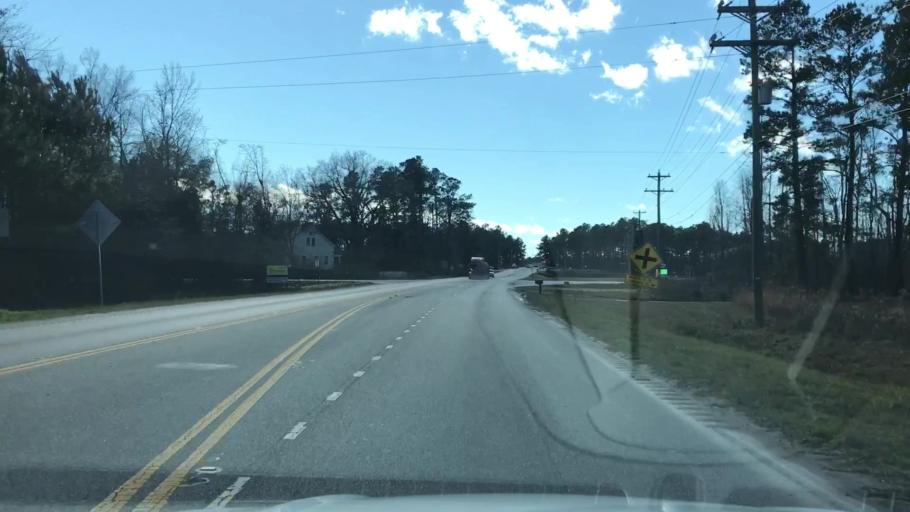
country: US
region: South Carolina
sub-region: Dorchester County
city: Summerville
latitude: 33.0849
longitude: -80.2036
